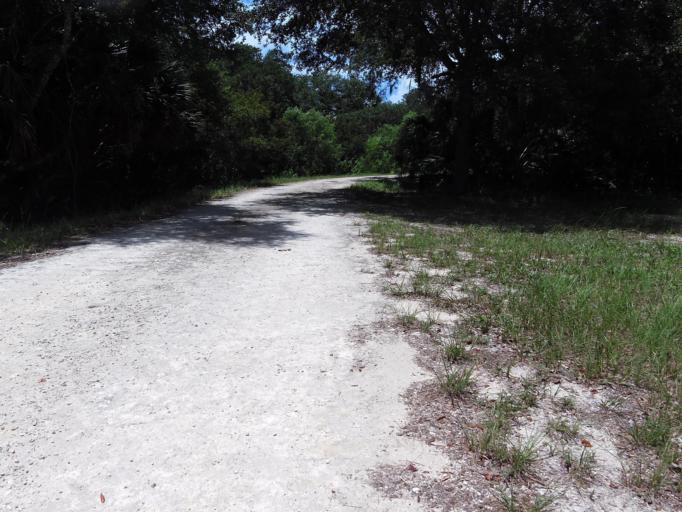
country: US
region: Florida
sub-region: Saint Johns County
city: Villano Beach
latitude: 30.0347
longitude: -81.3386
